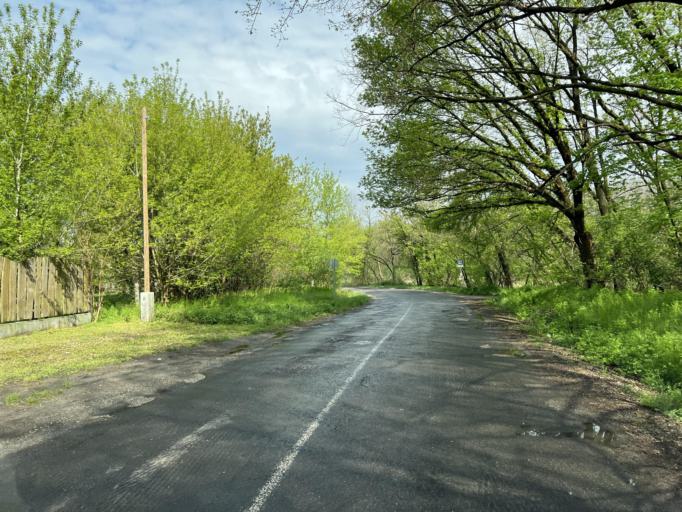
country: HU
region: Pest
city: Danszentmiklos
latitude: 47.1622
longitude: 19.5052
